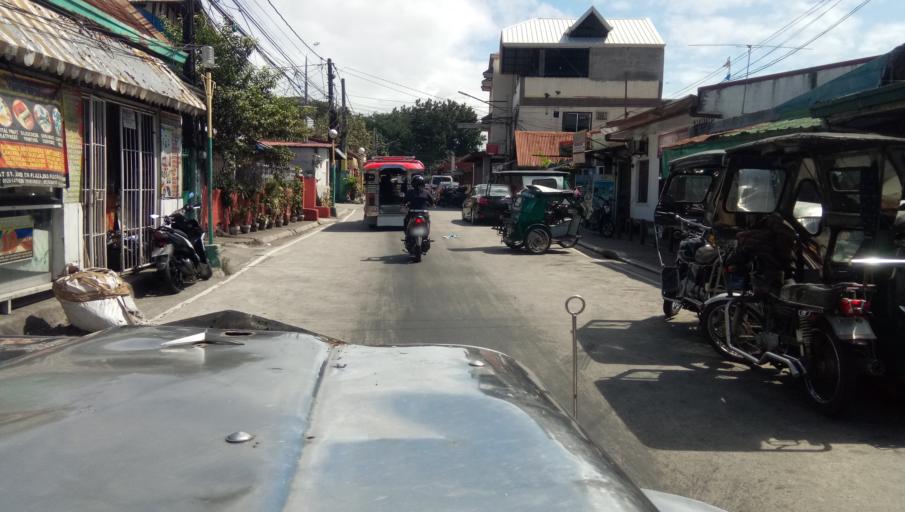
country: PH
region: Calabarzon
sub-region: Province of Cavite
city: Dasmarinas
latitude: 14.3261
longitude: 120.9354
